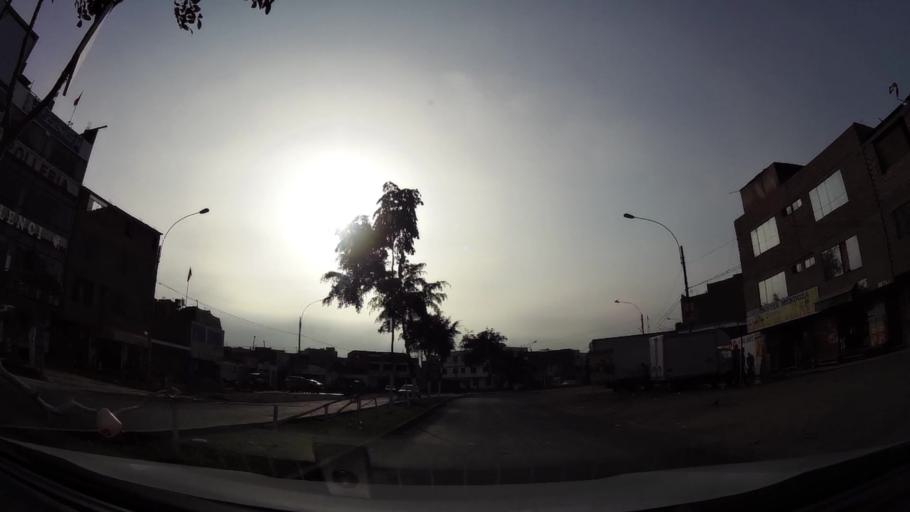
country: PE
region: Lima
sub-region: Lima
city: Independencia
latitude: -11.9955
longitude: -77.1045
